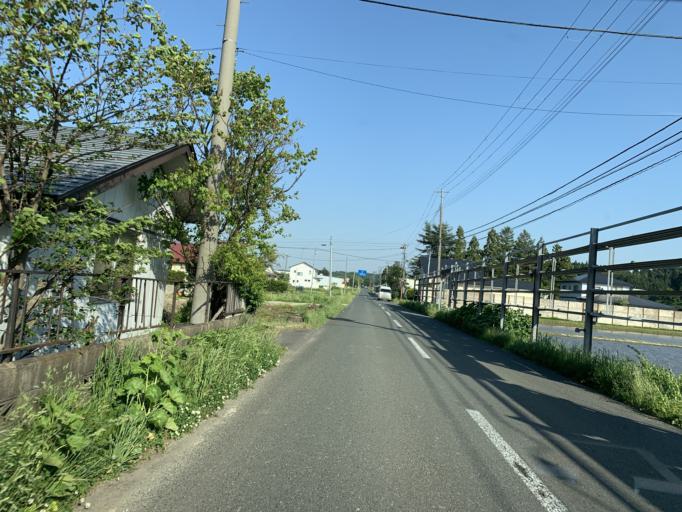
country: JP
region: Iwate
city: Kitakami
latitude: 39.2911
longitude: 140.9963
